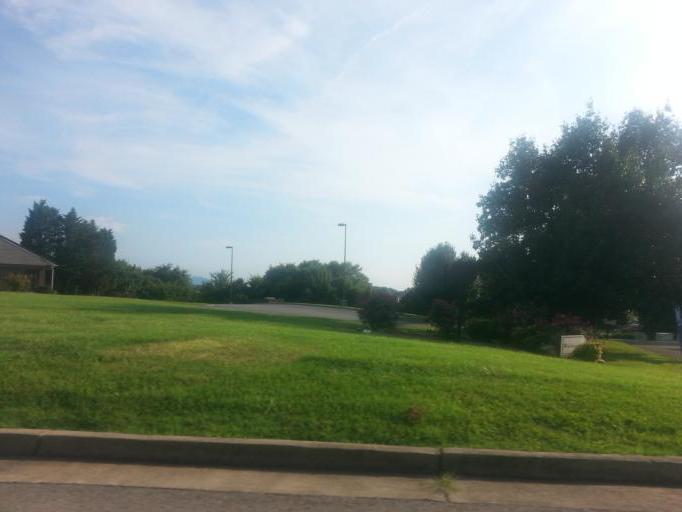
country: US
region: Tennessee
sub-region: Sevier County
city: Seymour
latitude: 35.8650
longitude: -83.7480
